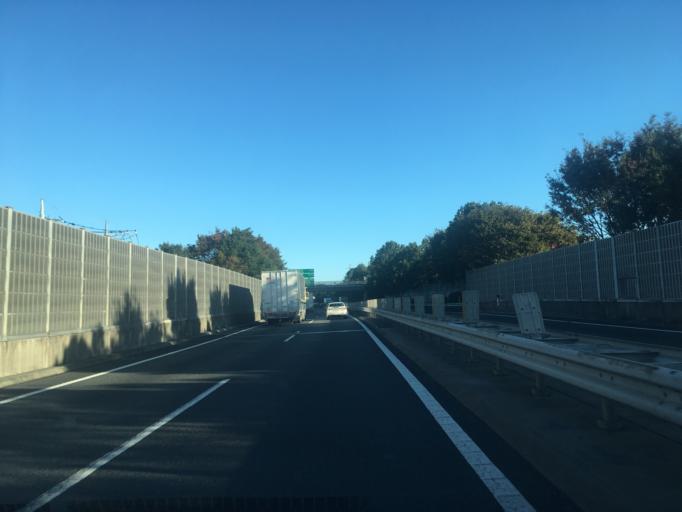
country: JP
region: Saitama
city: Sayama
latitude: 35.8254
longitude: 139.3738
